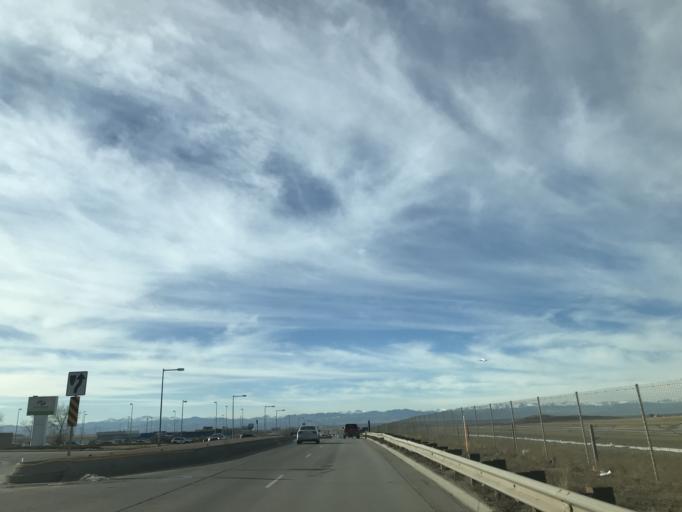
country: US
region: Colorado
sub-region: Adams County
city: Aurora
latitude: 39.8383
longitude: -104.7080
